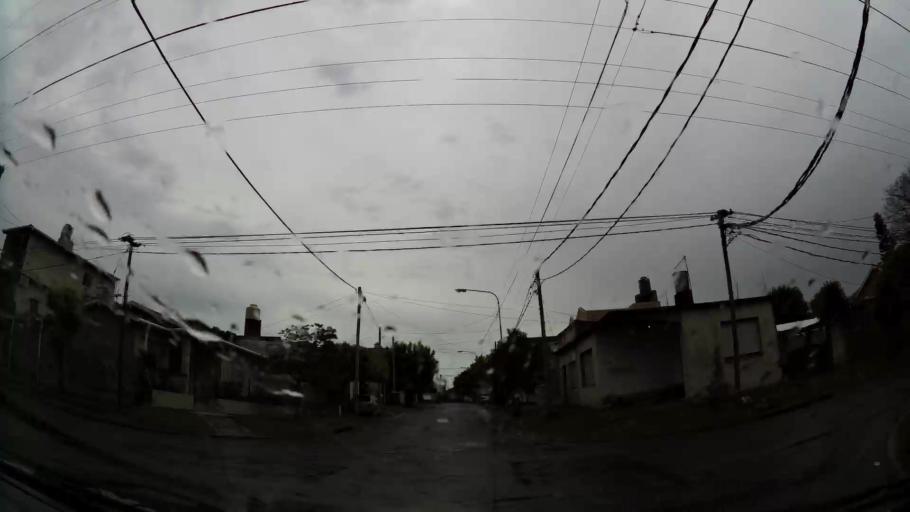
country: AR
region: Buenos Aires
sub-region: Partido de Quilmes
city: Quilmes
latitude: -34.7616
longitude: -58.2196
